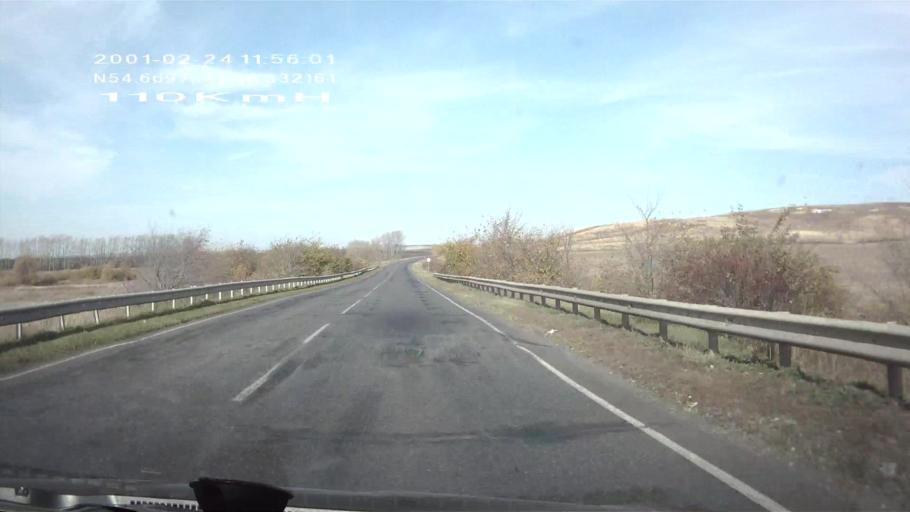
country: RU
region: Mordoviya
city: Ardatov
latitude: 54.6708
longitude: 46.2331
